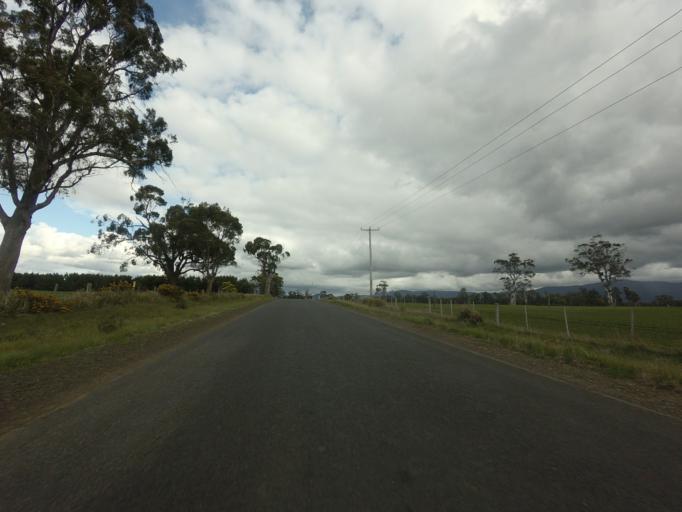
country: AU
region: Tasmania
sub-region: Northern Midlands
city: Longford
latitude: -41.7618
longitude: 147.0831
